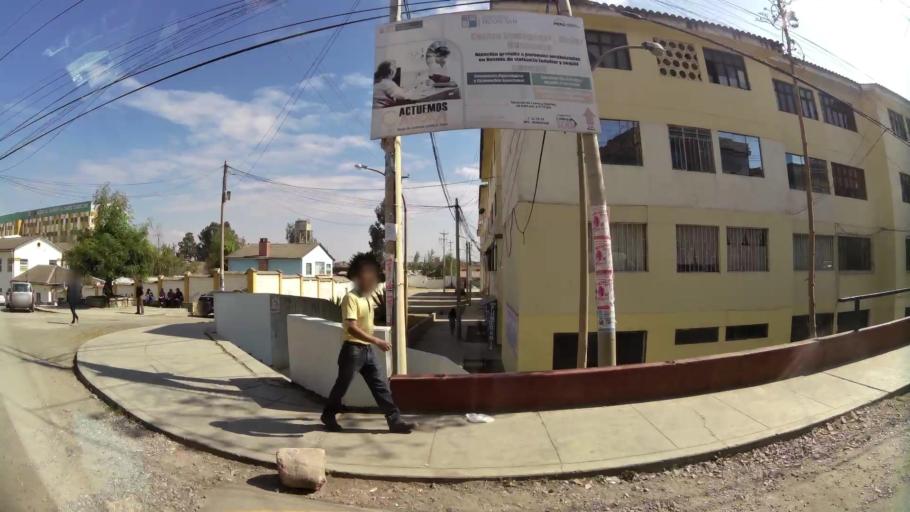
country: PE
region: Junin
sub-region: Provincia de Huancayo
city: El Tambo
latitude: -12.0730
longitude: -75.2201
